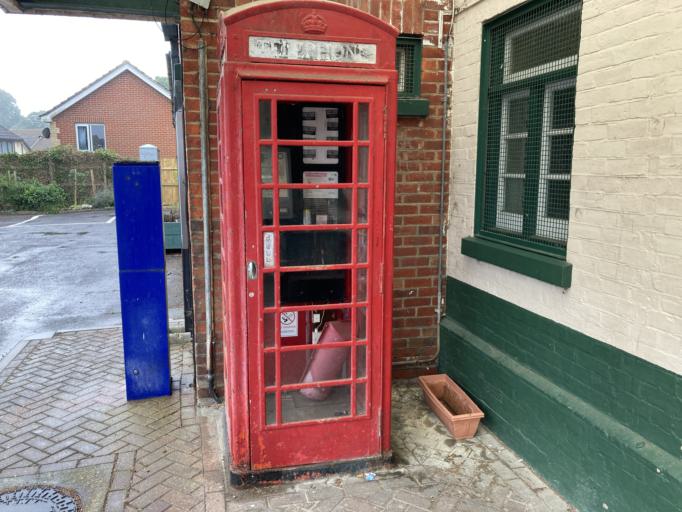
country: GB
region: England
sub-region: Isle of Wight
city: Sandown
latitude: 50.6568
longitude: -1.1622
